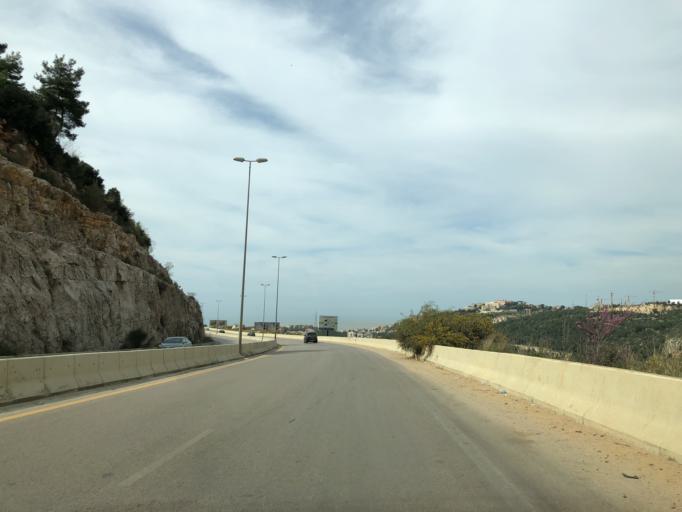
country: LB
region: Mont-Liban
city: Jdaidet el Matn
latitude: 33.8984
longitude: 35.6473
